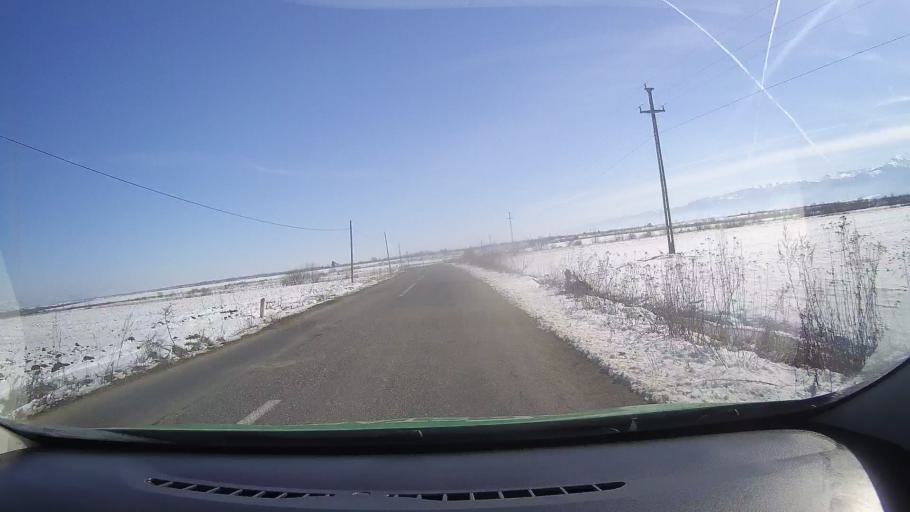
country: RO
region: Brasov
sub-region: Comuna Dragus
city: Dragus
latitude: 45.7628
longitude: 24.7987
